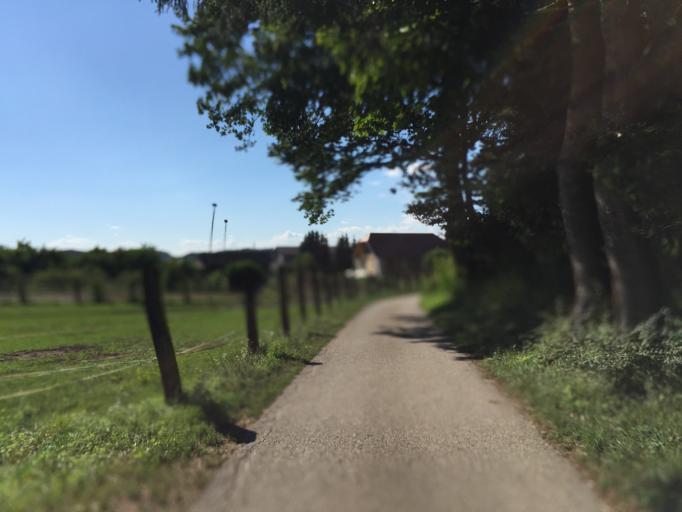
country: AT
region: Carinthia
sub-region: Politischer Bezirk Volkermarkt
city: Feistritz ob Bleiburg
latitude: 46.5594
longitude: 14.7418
